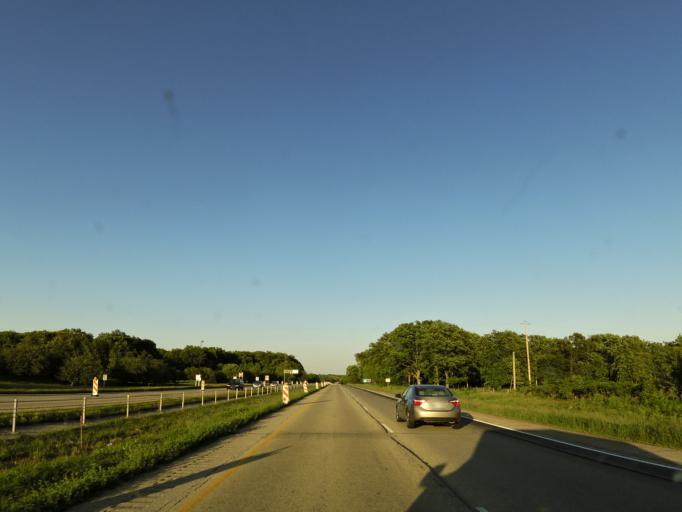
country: US
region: Illinois
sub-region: Vermilion County
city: Oakwood
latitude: 40.1278
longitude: -87.7451
